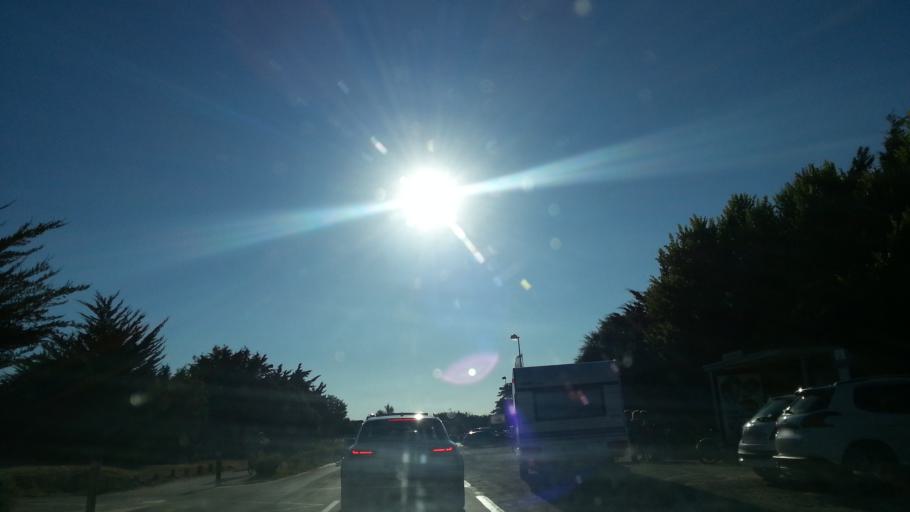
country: FR
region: Poitou-Charentes
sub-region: Departement de la Charente-Maritime
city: Dolus-d'Oleron
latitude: 45.9013
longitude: -1.2946
